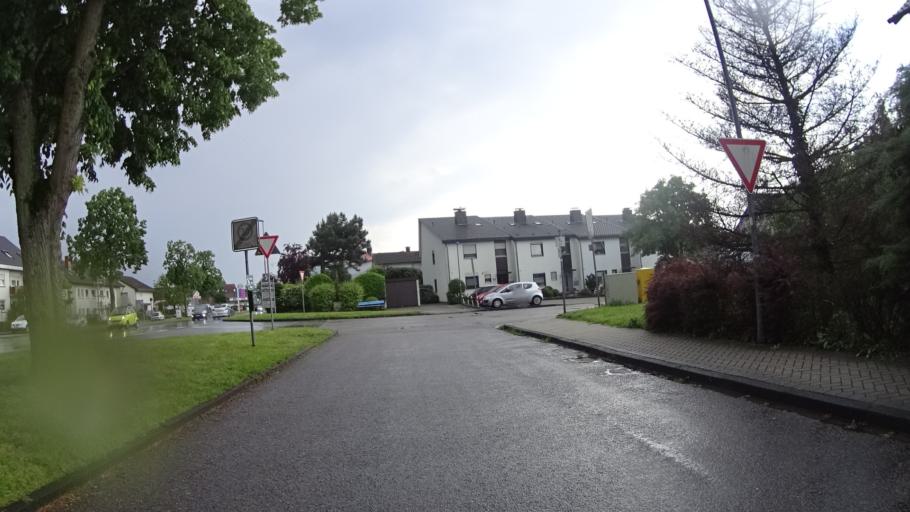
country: DE
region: Baden-Wuerttemberg
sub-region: Karlsruhe Region
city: Durmersheim
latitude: 48.9400
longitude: 8.2749
